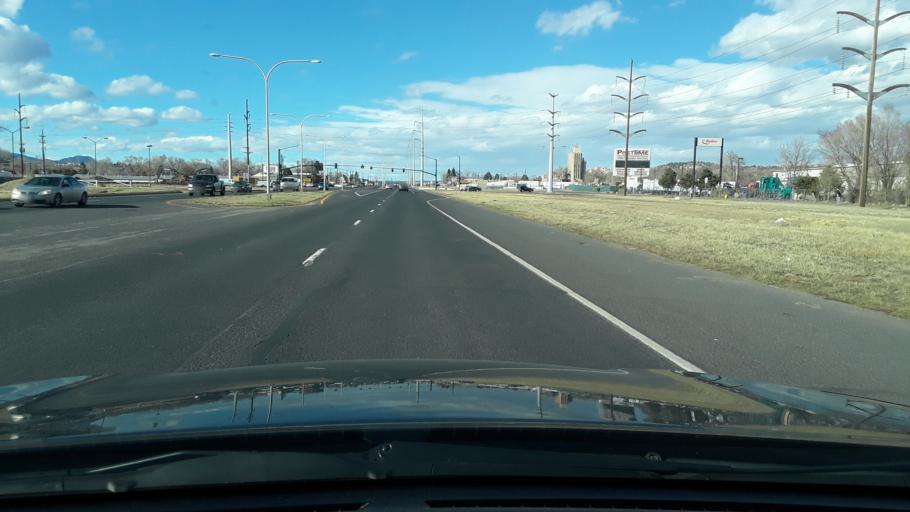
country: US
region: Colorado
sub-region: El Paso County
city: Colorado Springs
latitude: 38.8840
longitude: -104.8187
